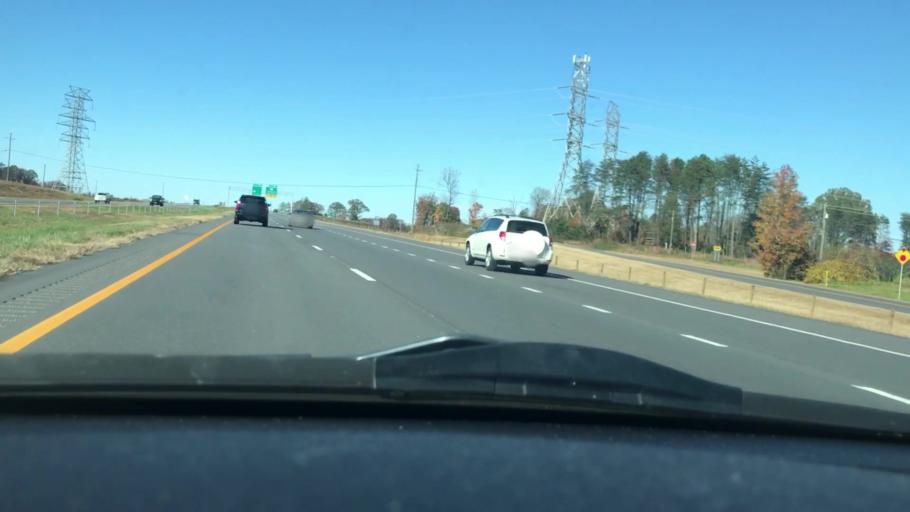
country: US
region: North Carolina
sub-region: Guilford County
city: Summerfield
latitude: 36.2404
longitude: -79.9184
